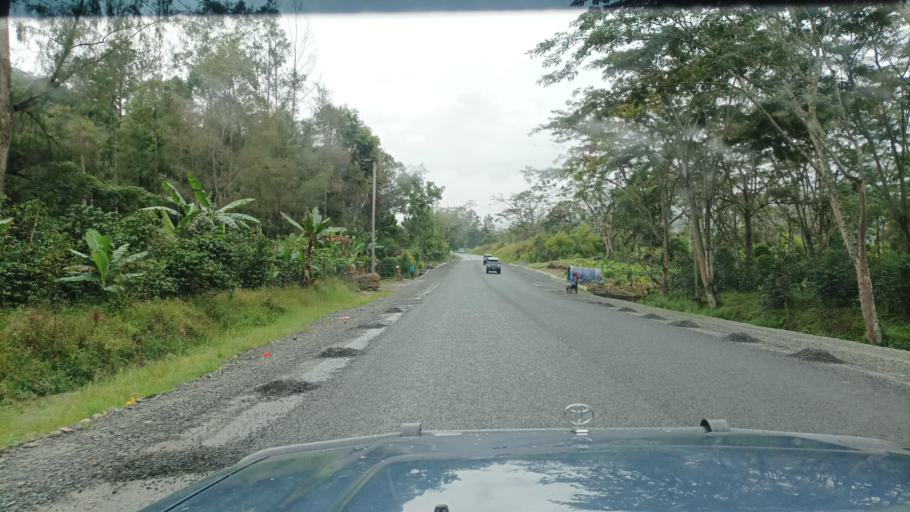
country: PG
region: Western Highlands
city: Rauna
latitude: -5.8332
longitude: 144.3534
